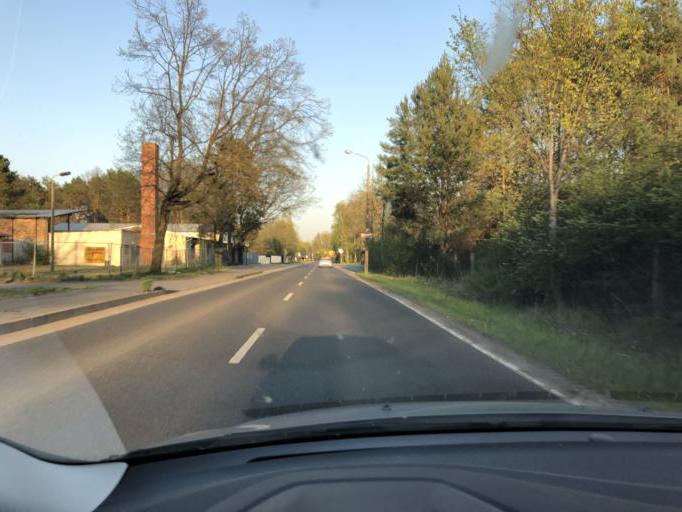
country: DE
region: Brandenburg
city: Spremberg
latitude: 51.5244
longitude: 14.3293
